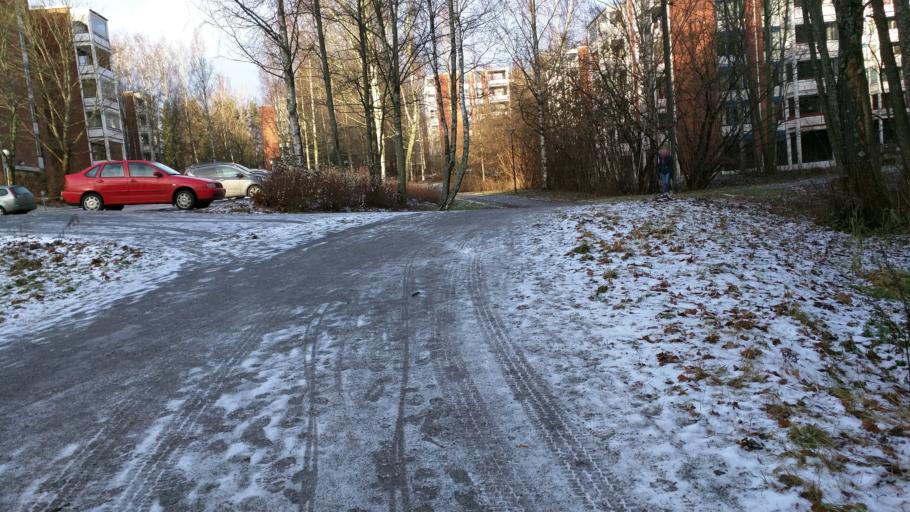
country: FI
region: Uusimaa
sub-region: Helsinki
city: Kilo
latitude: 60.2608
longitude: 24.8088
